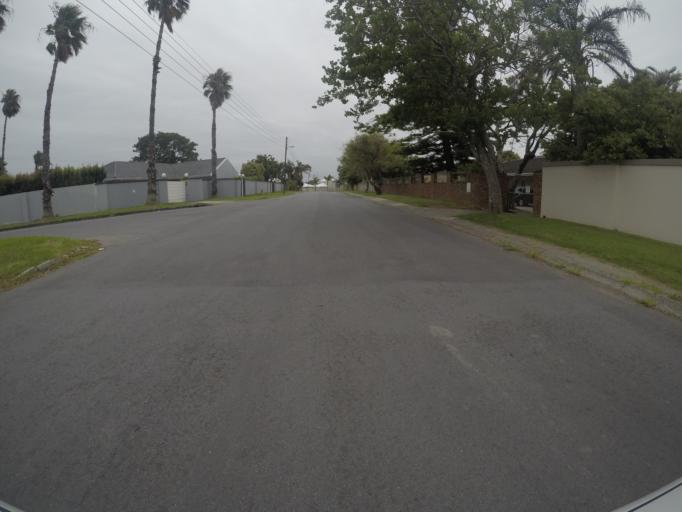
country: ZA
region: Eastern Cape
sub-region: Buffalo City Metropolitan Municipality
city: East London
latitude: -32.9619
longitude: 27.9335
